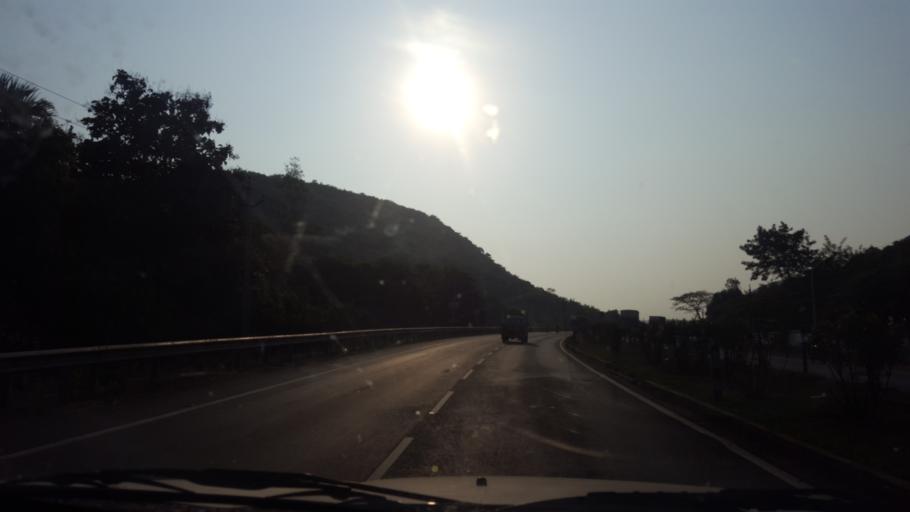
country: IN
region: Andhra Pradesh
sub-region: East Godavari
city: Tuni
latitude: 17.3014
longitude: 82.4350
